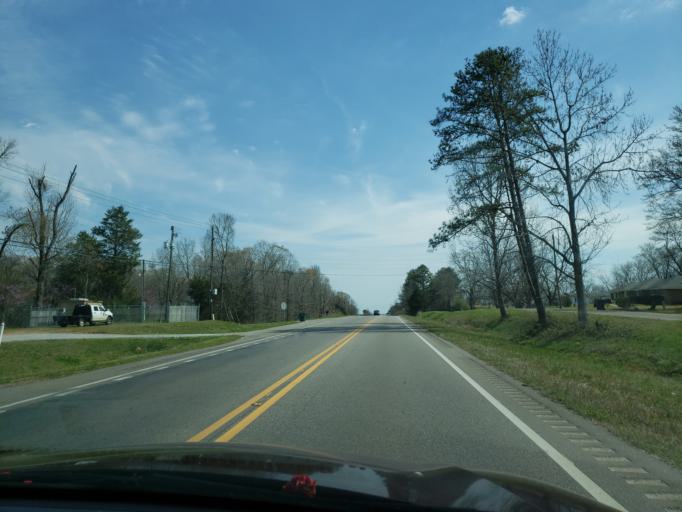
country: US
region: Alabama
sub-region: Autauga County
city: Prattville
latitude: 32.4305
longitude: -86.5374
